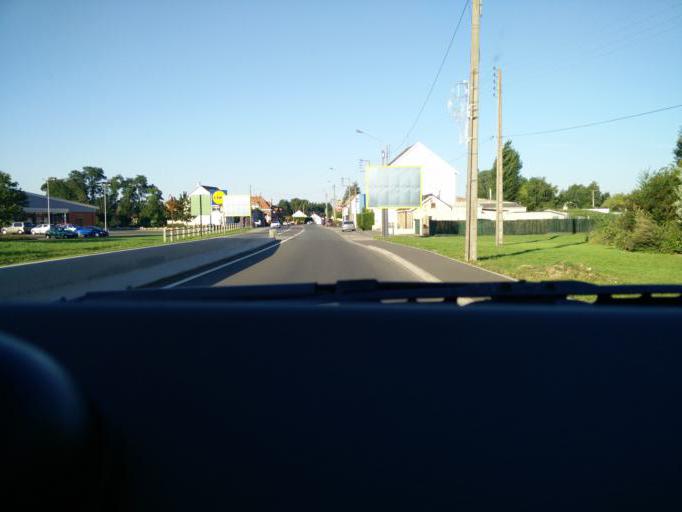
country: FR
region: Nord-Pas-de-Calais
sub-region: Departement du Pas-de-Calais
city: Auchy-les-Mines
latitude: 50.5205
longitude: 2.7920
